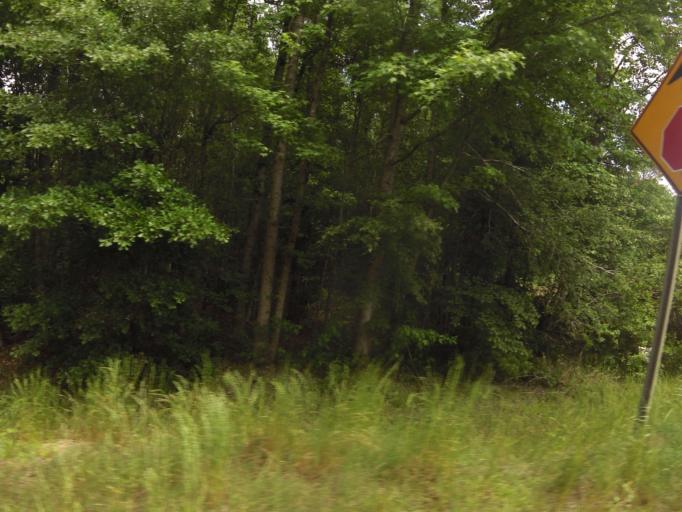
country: US
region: Georgia
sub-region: Candler County
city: Metter
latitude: 32.3785
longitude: -82.1670
